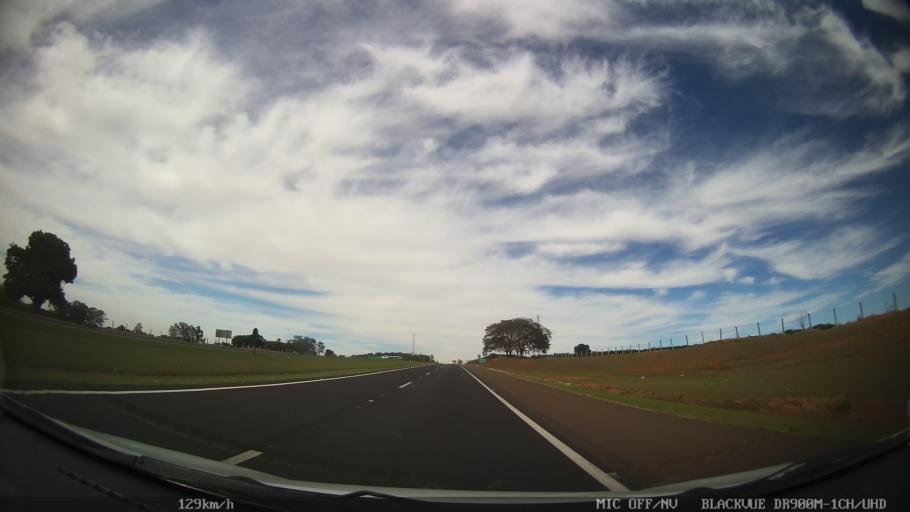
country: BR
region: Sao Paulo
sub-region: Taquaritinga
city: Taquaritinga
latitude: -21.4968
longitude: -48.5682
